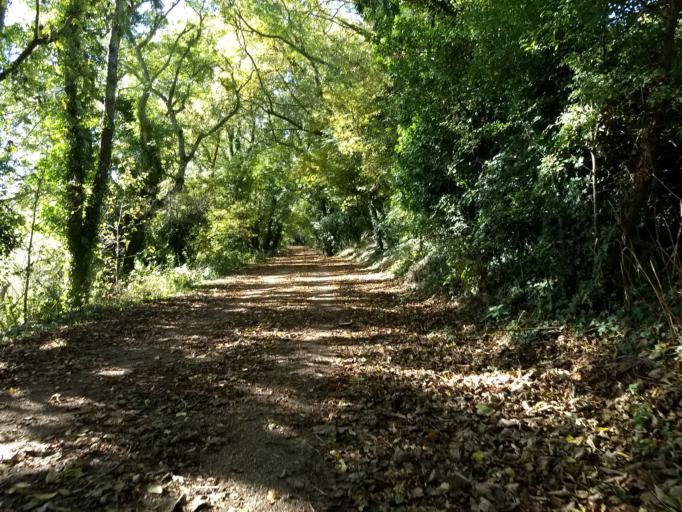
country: GB
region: England
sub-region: Isle of Wight
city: Ventnor
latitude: 50.6278
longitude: -1.2184
